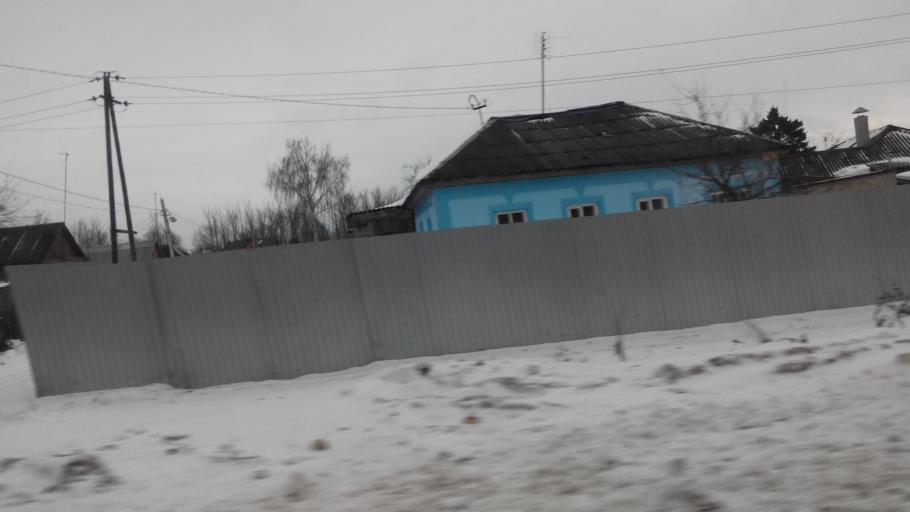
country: RU
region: Tula
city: Uzlovaya
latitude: 53.9791
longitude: 38.1905
